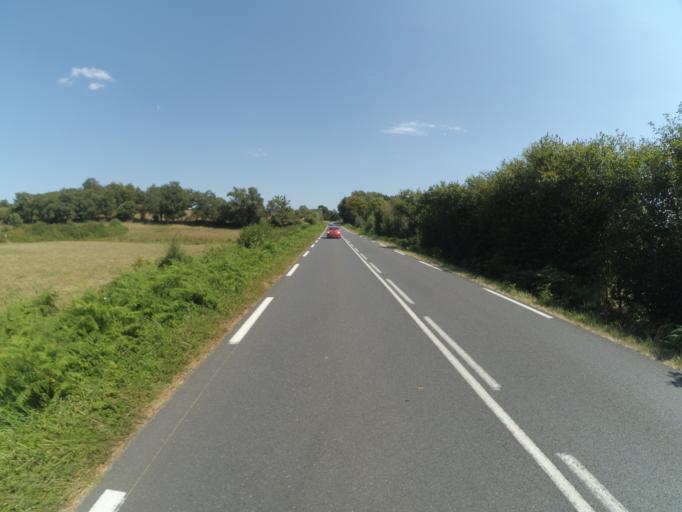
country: FR
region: Limousin
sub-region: Departement de la Haute-Vienne
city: Magnac-Laval
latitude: 46.2150
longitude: 1.1295
